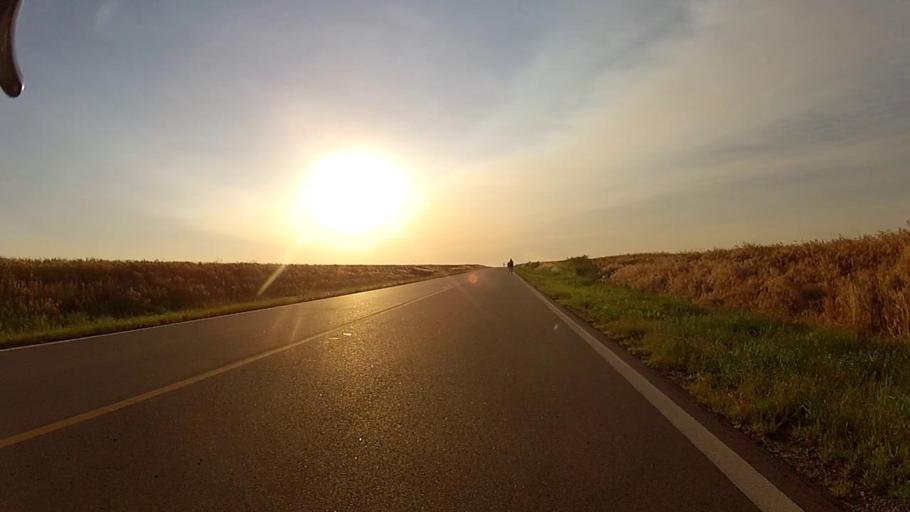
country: US
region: Kansas
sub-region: Harper County
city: Anthony
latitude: 37.1531
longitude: -97.9195
